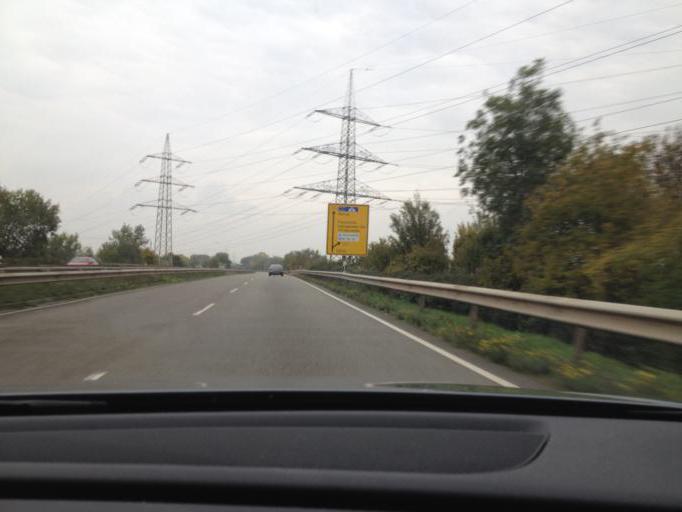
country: DE
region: Rheinland-Pfalz
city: Frankenthal
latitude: 49.5287
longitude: 8.4051
